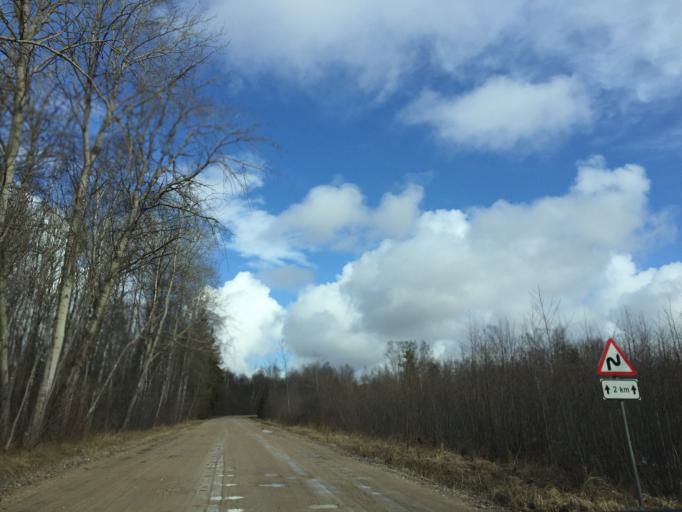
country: EE
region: Laeaene
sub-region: Lihula vald
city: Lihula
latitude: 58.7175
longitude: 23.8239
